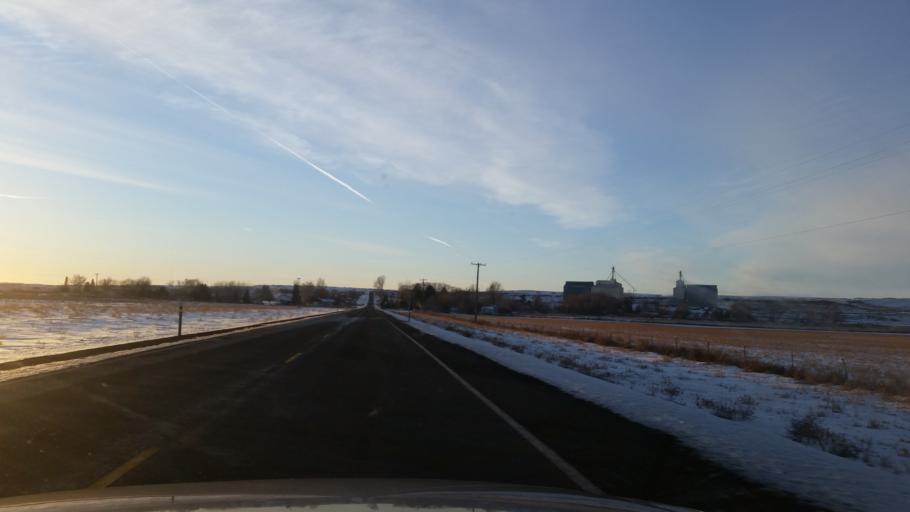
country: US
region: Washington
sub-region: Spokane County
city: Cheney
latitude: 47.1170
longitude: -117.7215
